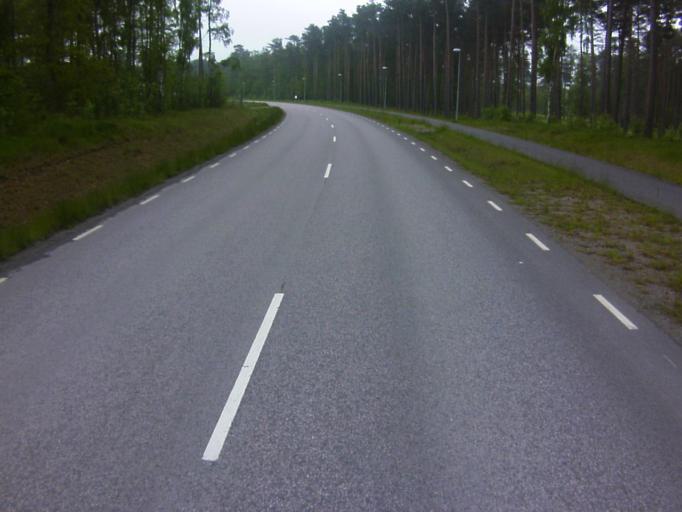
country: SE
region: Blekinge
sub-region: Solvesborgs Kommun
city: Soelvesborg
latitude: 56.0460
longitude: 14.6094
